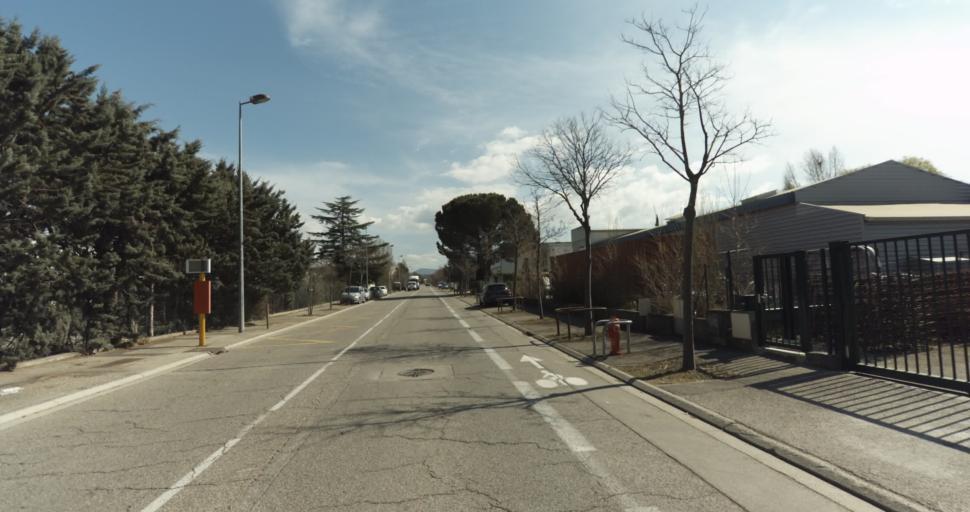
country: FR
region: Provence-Alpes-Cote d'Azur
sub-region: Departement des Bouches-du-Rhone
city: Cabries
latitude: 43.4846
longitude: 5.3742
